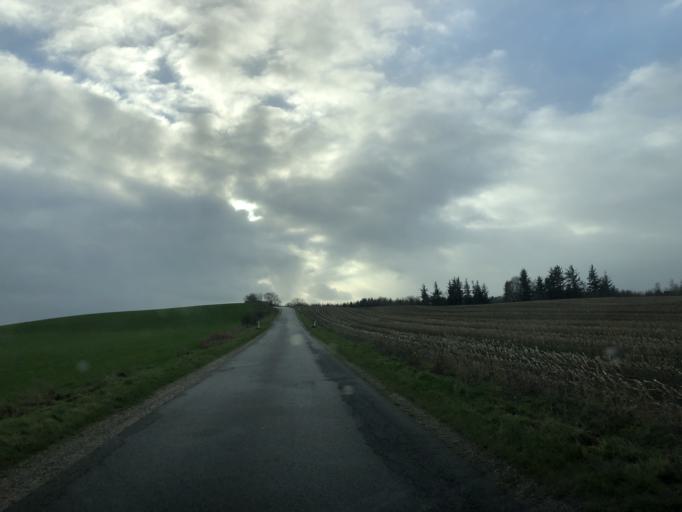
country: DK
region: North Denmark
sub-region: Rebild Kommune
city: Stovring
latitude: 56.9147
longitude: 9.7808
